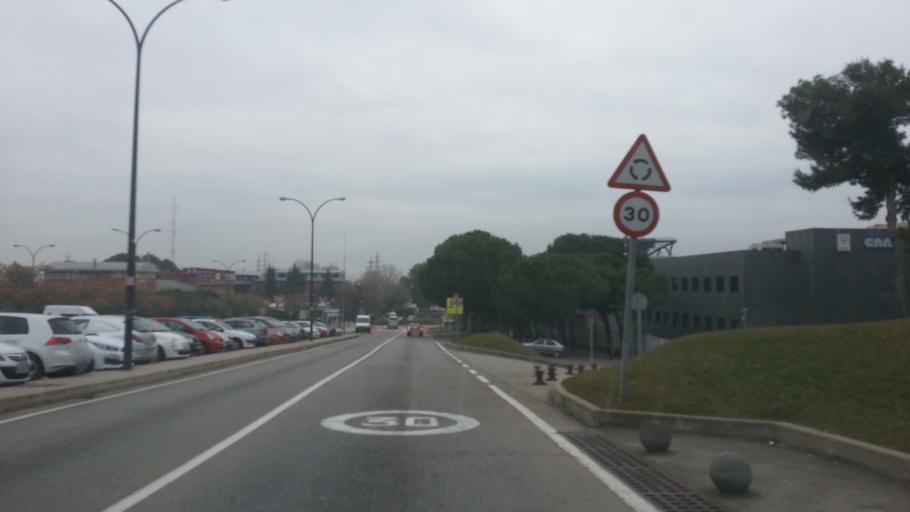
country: ES
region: Catalonia
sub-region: Provincia de Barcelona
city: Barbera del Valles
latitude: 41.5031
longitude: 2.1094
